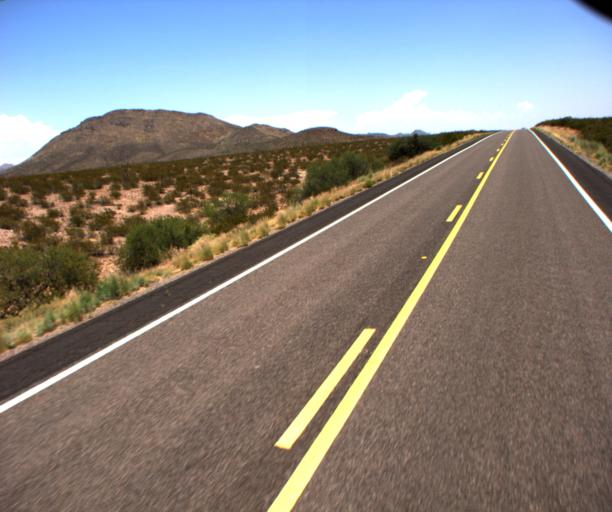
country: US
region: Arizona
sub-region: Graham County
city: Swift Trail Junction
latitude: 32.7521
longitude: -109.4083
